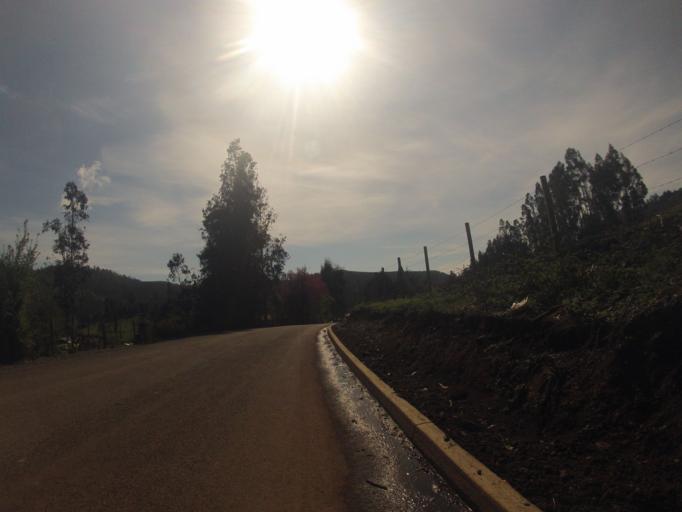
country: CL
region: Araucania
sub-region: Provincia de Cautin
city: Temuco
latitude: -38.6866
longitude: -72.5845
